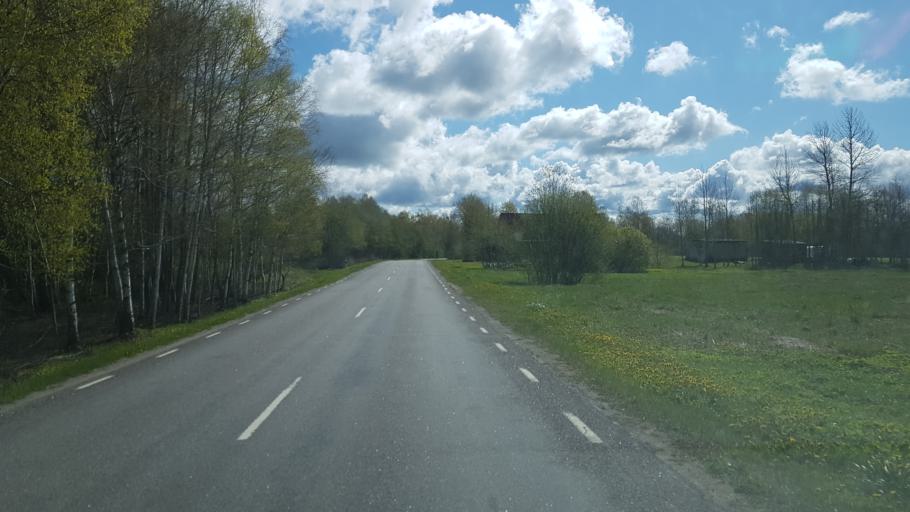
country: EE
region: Raplamaa
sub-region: Kehtna vald
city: Kehtna
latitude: 59.0535
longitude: 25.0107
